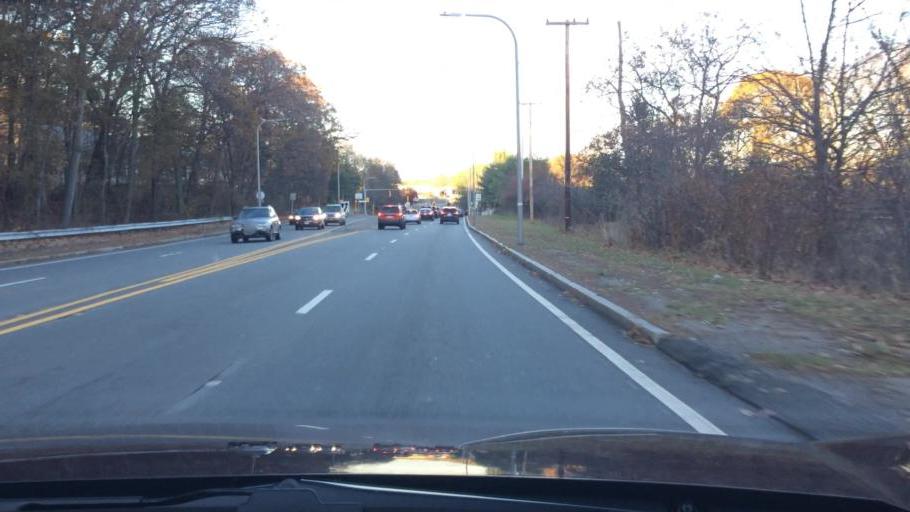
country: US
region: Massachusetts
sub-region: Norfolk County
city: Norwood
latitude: 42.2121
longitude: -71.1917
